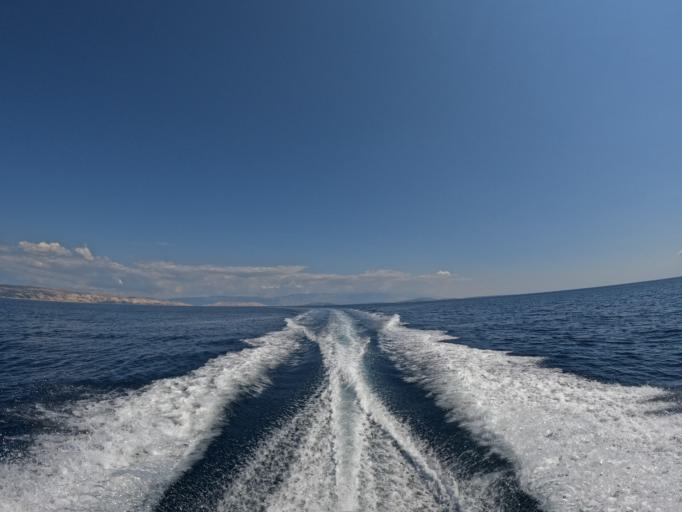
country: HR
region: Primorsko-Goranska
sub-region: Grad Krk
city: Krk
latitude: 44.9296
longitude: 14.5251
